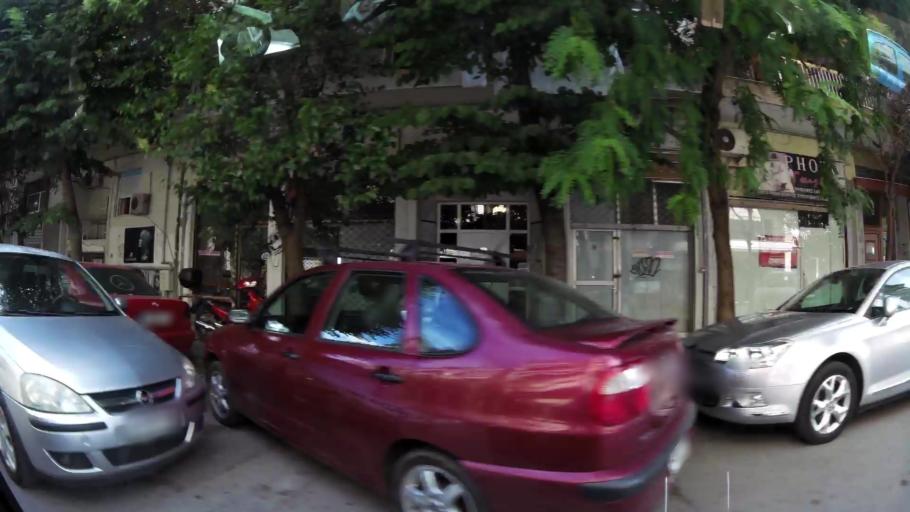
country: GR
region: Central Macedonia
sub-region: Nomos Thessalonikis
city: Triandria
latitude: 40.6023
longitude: 22.9620
